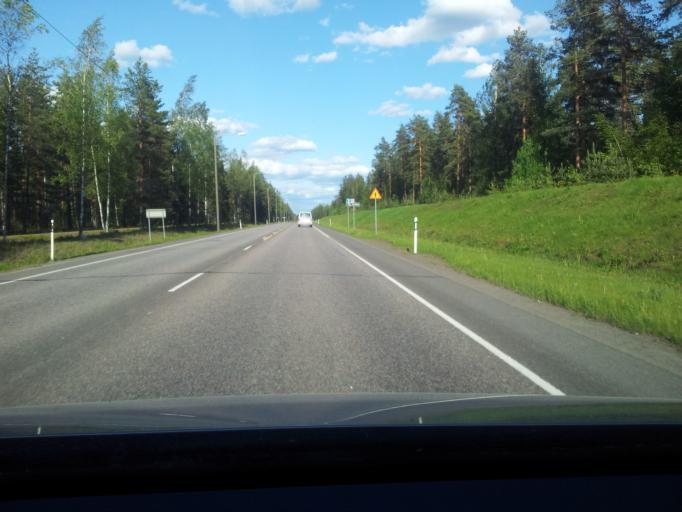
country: FI
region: Kymenlaakso
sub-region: Kouvola
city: Kouvola
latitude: 60.8873
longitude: 26.8651
